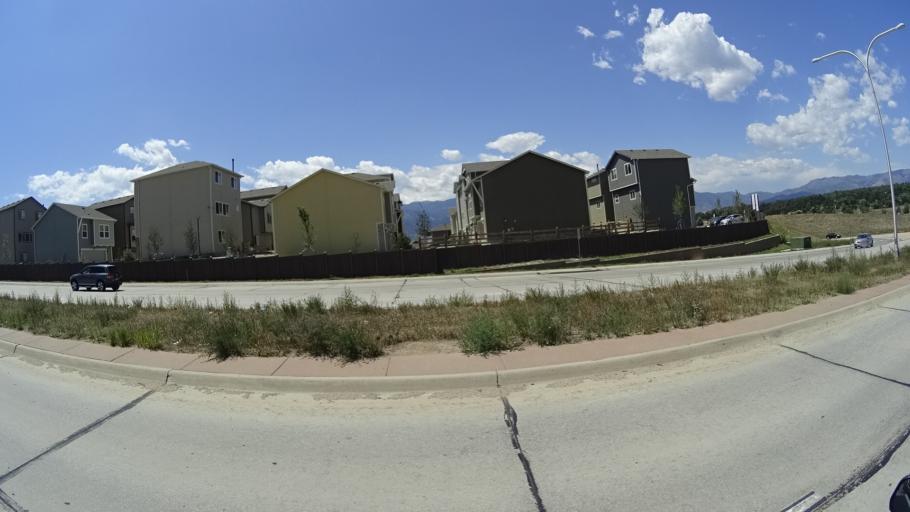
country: US
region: Colorado
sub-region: El Paso County
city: Stratmoor
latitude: 38.8095
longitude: -104.7876
